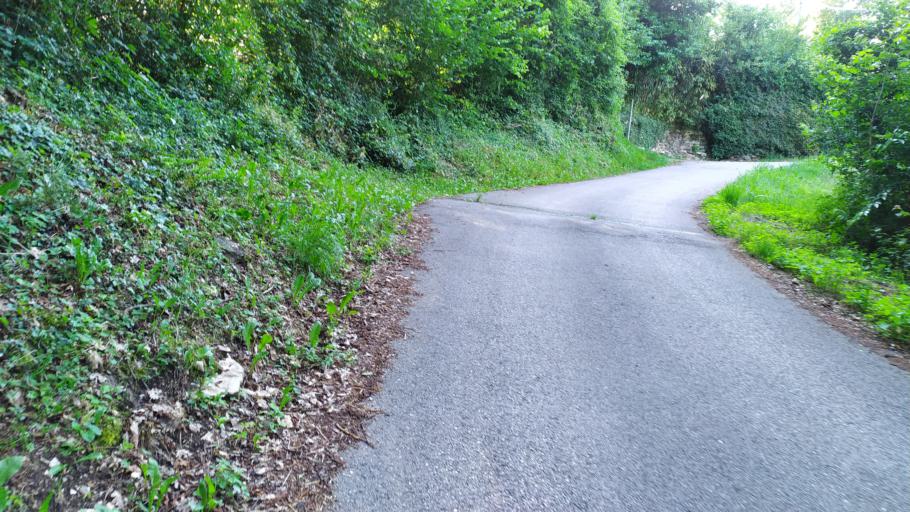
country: IT
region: Veneto
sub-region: Provincia di Vicenza
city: Schio
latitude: 45.6858
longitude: 11.3475
